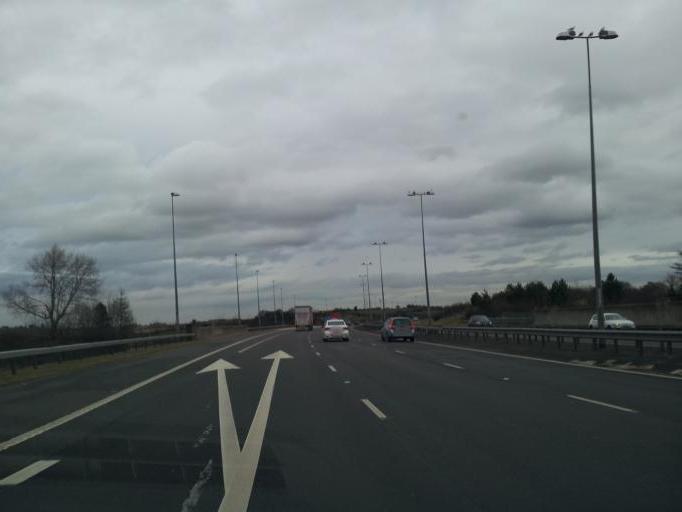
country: GB
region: England
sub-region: Staffordshire
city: Chasetown
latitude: 52.6620
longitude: -1.9345
